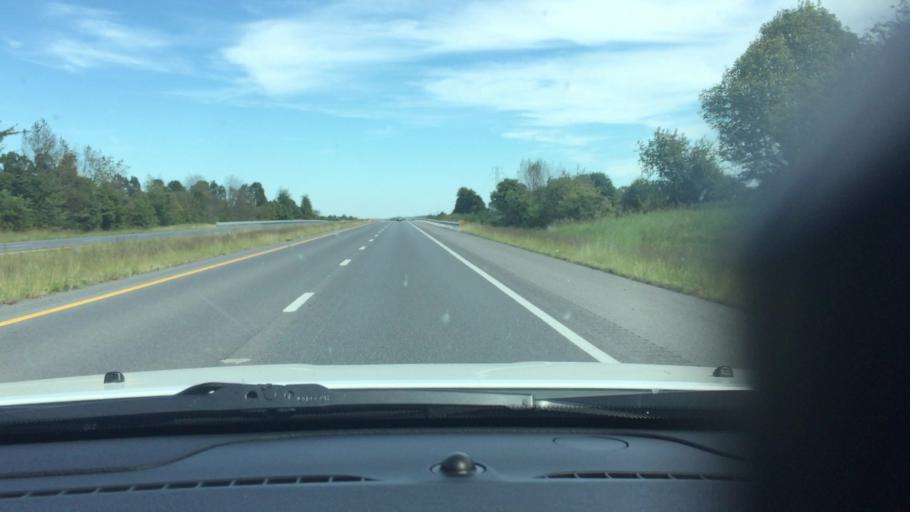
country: US
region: Kentucky
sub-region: Caldwell County
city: Princeton
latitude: 37.1103
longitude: -87.9477
